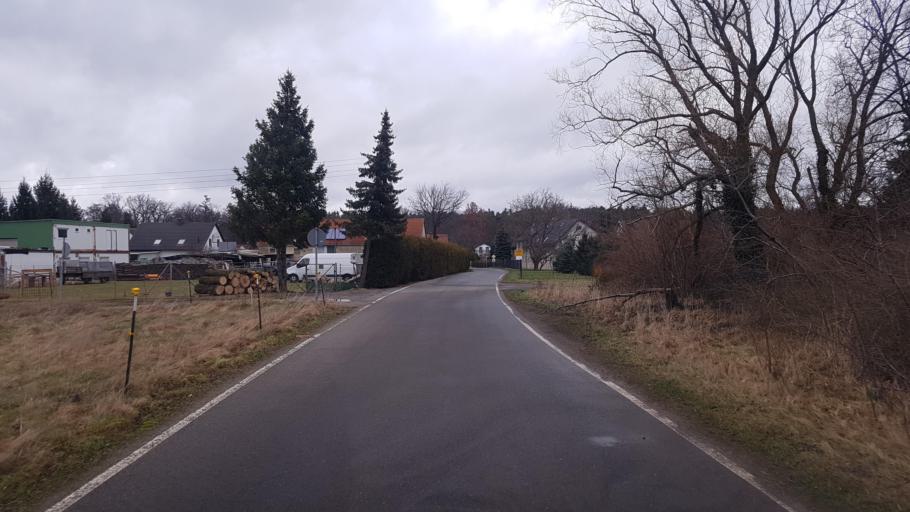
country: DE
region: Brandenburg
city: Kroppen
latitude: 51.3781
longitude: 13.7959
